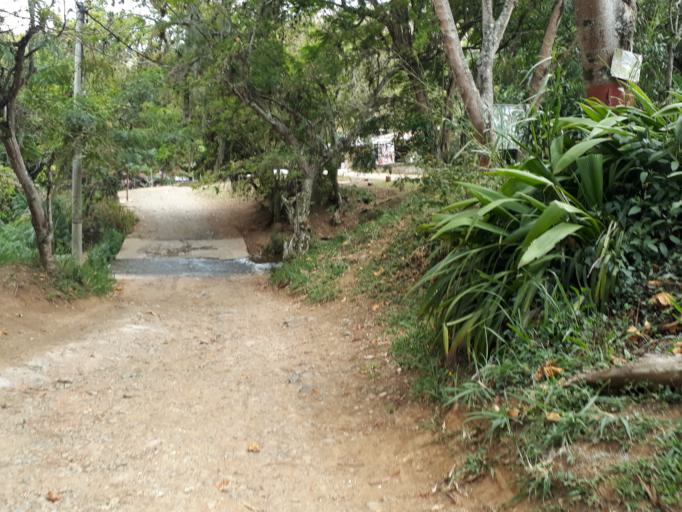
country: CO
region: Valle del Cauca
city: Cali
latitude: 3.4489
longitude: -76.5697
